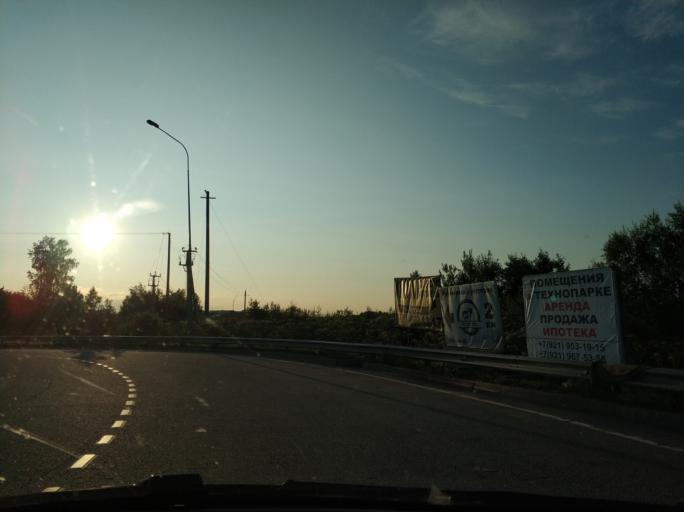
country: RU
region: Leningrad
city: Bugry
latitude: 60.1019
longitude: 30.3807
